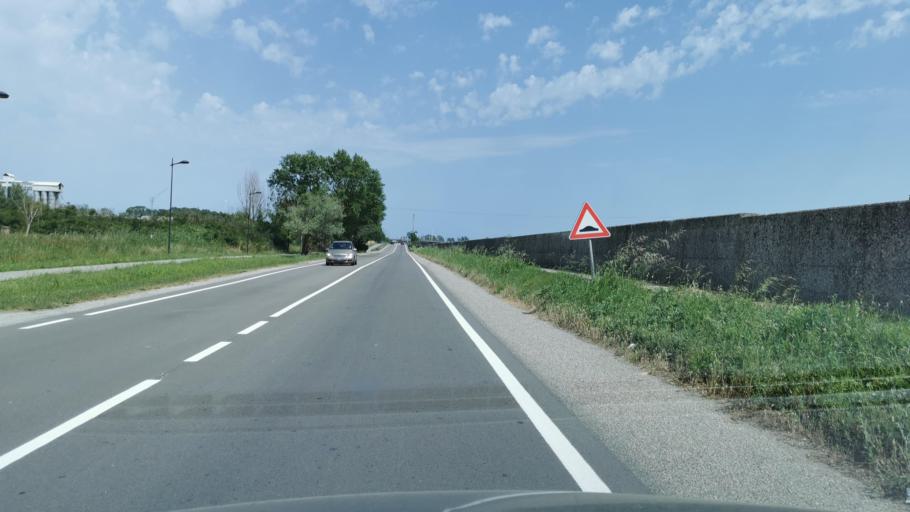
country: IT
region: Emilia-Romagna
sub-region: Provincia di Ferrara
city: Porto Garibaldi
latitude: 44.6764
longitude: 12.2187
